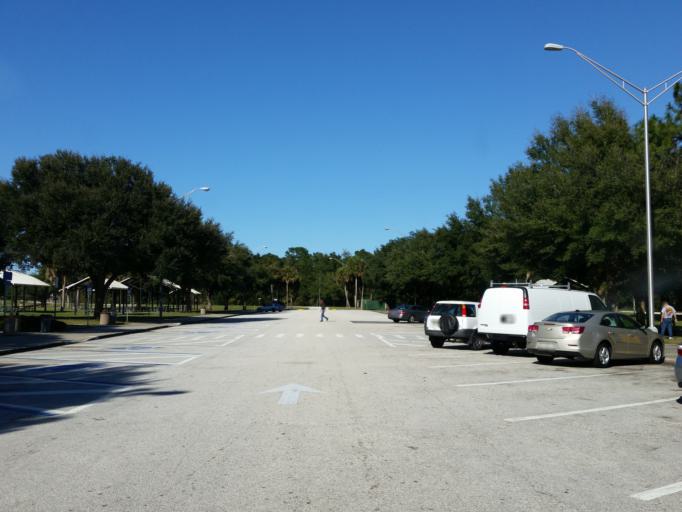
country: US
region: Florida
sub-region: Marion County
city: Ocala
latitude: 29.0927
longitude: -82.1835
